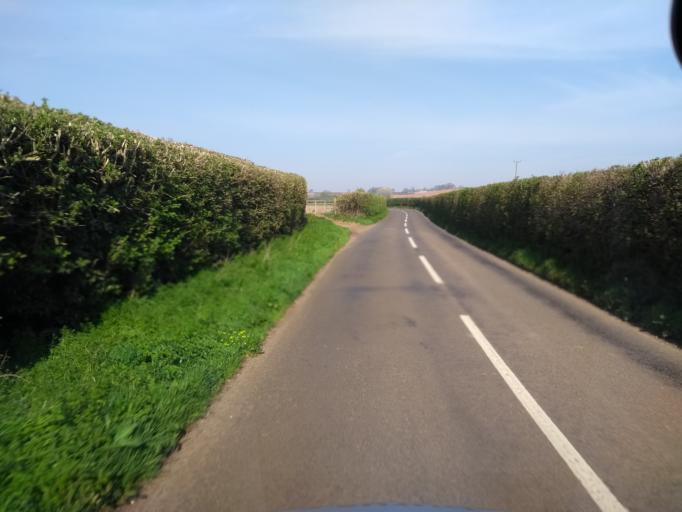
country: GB
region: England
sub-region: Somerset
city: Creech Saint Michael
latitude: 50.9925
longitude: -3.0082
